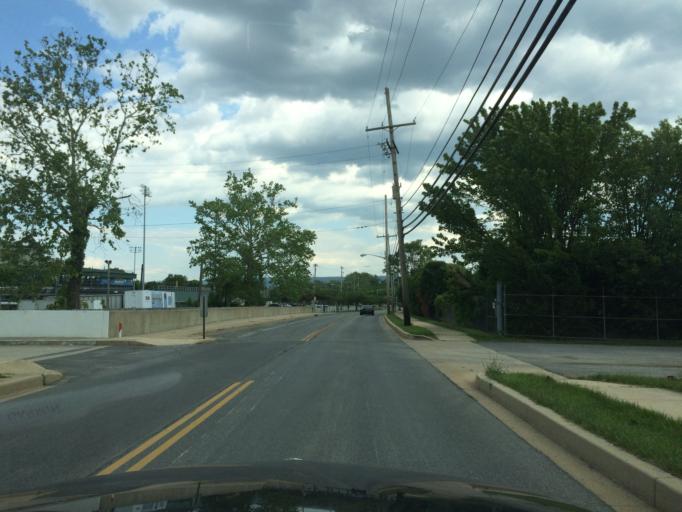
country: US
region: Maryland
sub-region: Washington County
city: Hagerstown
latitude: 39.6322
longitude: -77.7148
